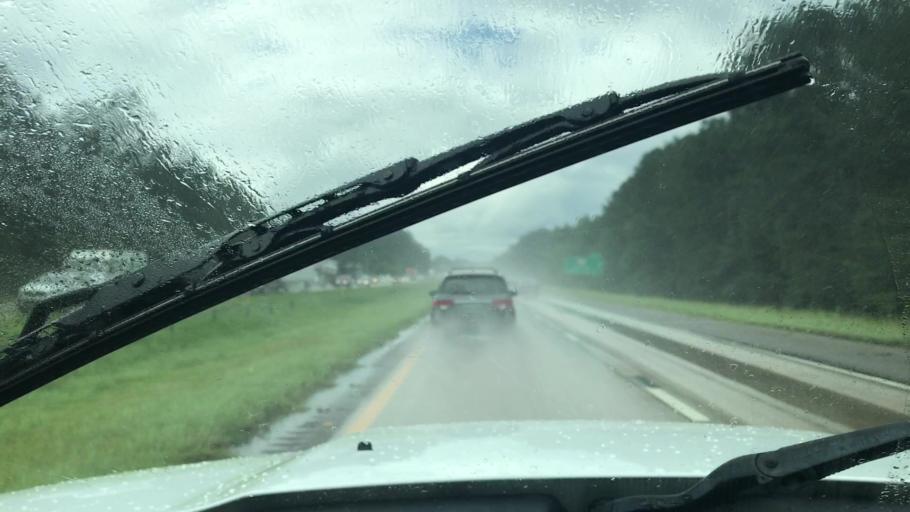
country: US
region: South Carolina
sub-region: Jasper County
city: Hardeeville
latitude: 32.3064
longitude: -81.0600
